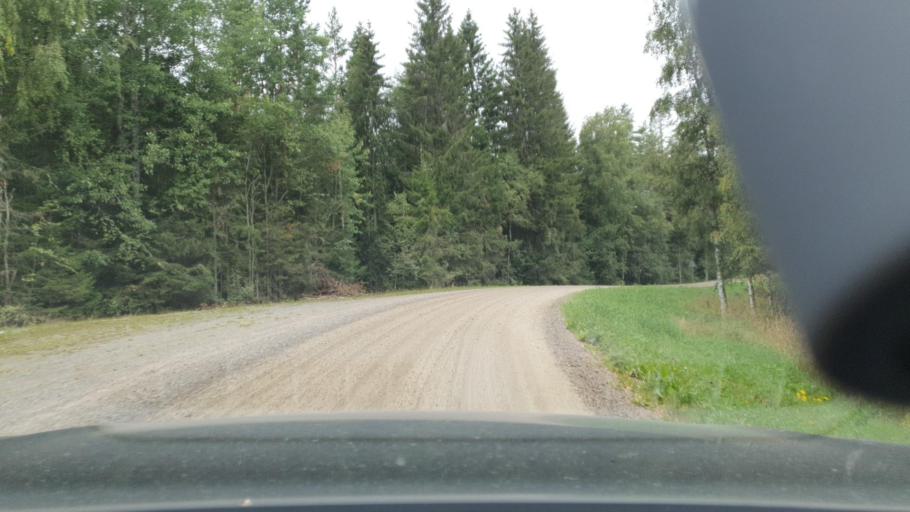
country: SE
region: Vaermland
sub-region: Eda Kommun
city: Charlottenberg
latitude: 60.0703
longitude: 12.5326
